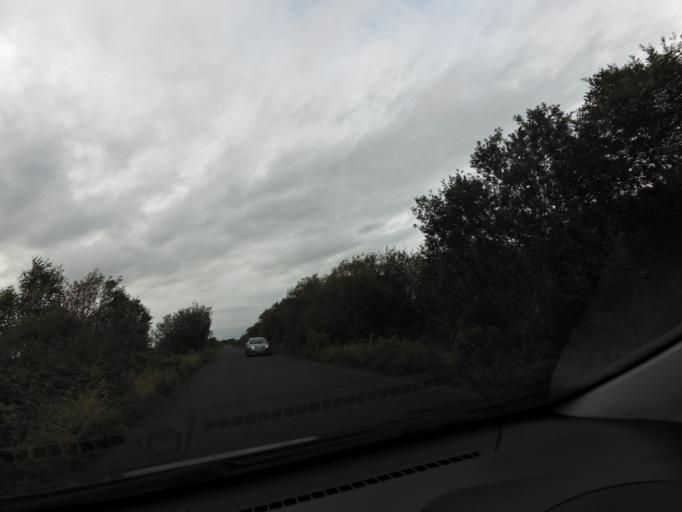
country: IE
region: Leinster
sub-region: Uibh Fhaili
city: Ferbane
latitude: 53.2398
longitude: -7.8272
